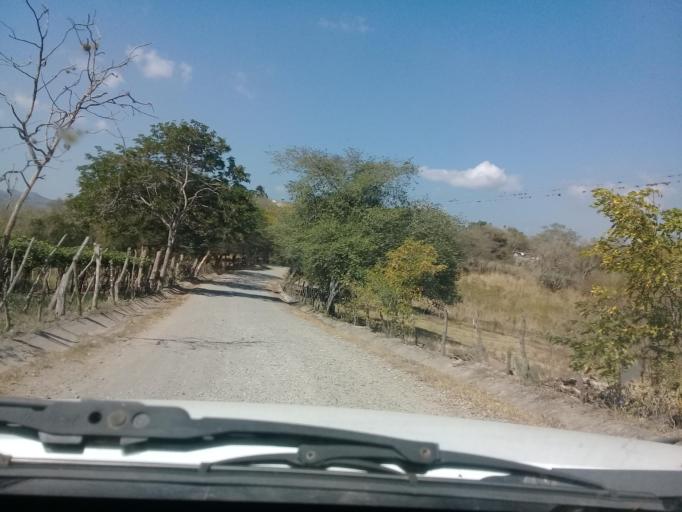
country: MX
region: Veracruz
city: Actopan
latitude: 19.4761
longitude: -96.6414
